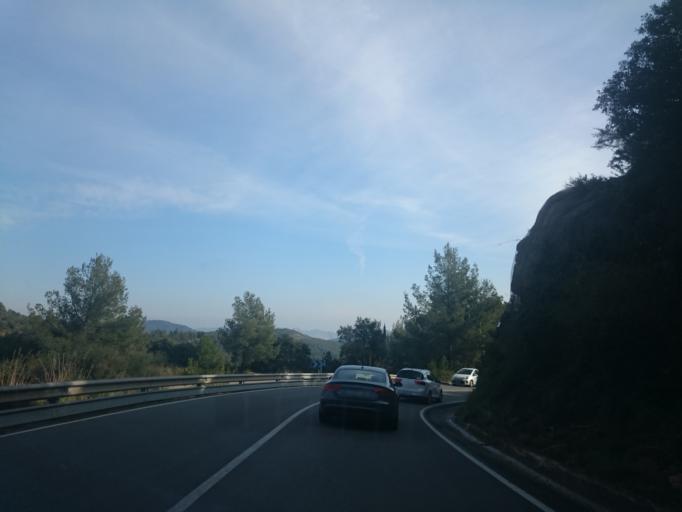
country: ES
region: Catalonia
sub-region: Provincia de Barcelona
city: Begues
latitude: 41.3157
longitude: 1.9581
